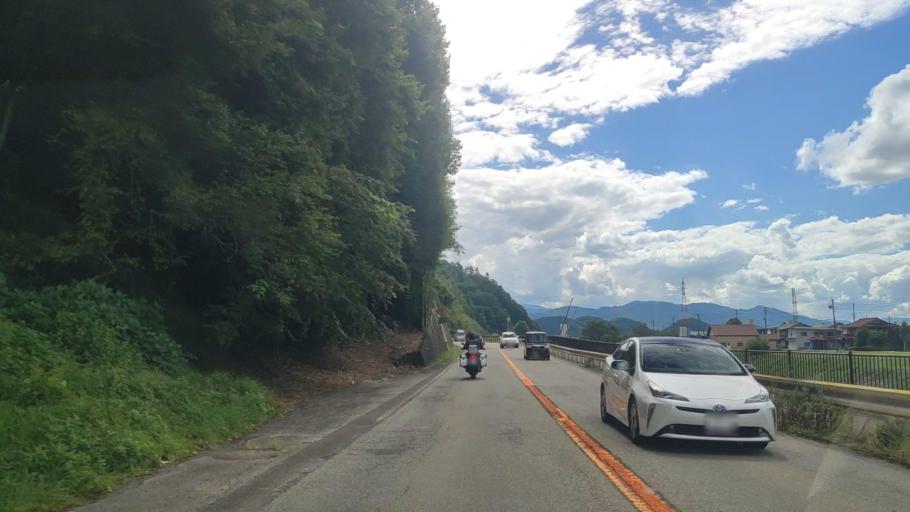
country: JP
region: Gifu
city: Takayama
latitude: 36.1791
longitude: 137.2499
